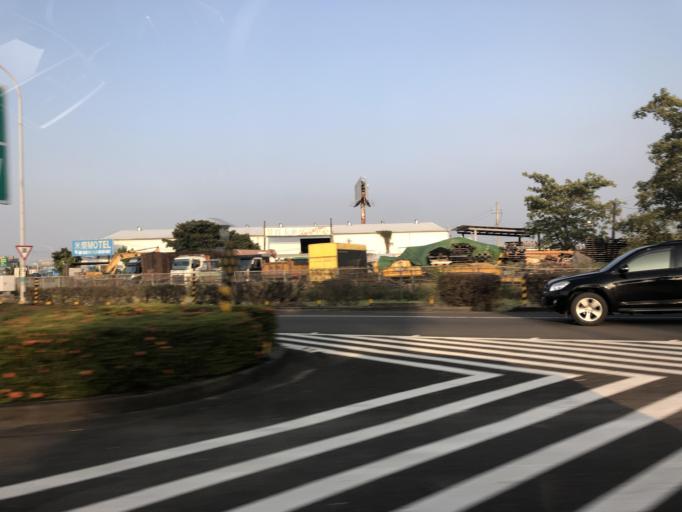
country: TW
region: Taiwan
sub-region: Tainan
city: Tainan
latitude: 23.1175
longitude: 120.2443
